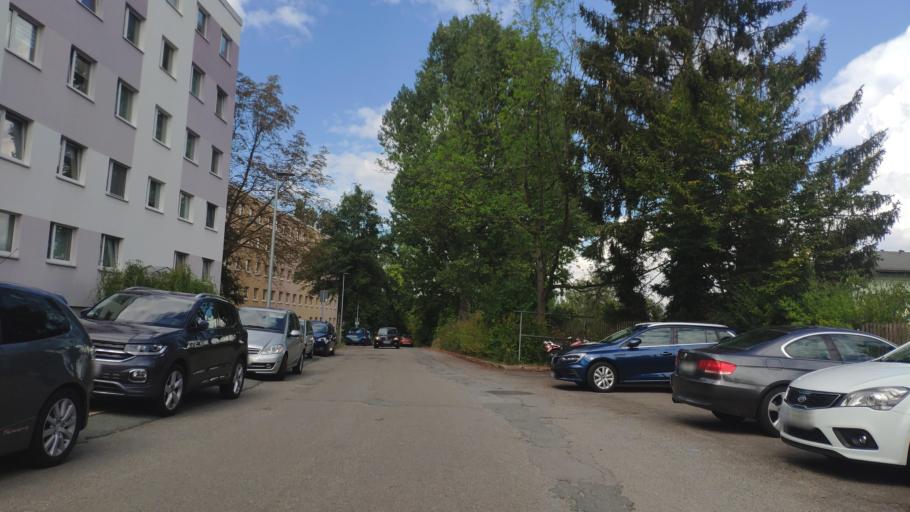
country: DE
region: Saxony
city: Chemnitz
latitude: 50.8160
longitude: 12.8936
